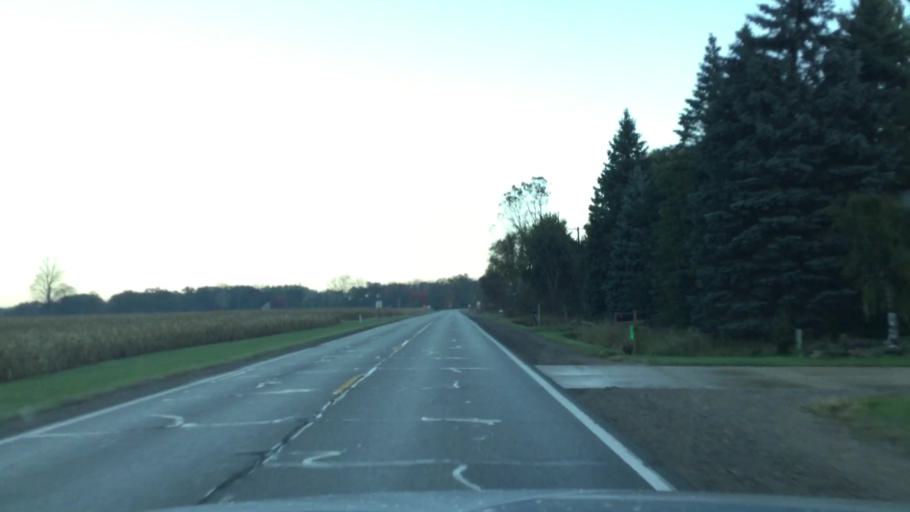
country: US
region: Michigan
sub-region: Livingston County
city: Howell
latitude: 42.6374
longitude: -83.9322
